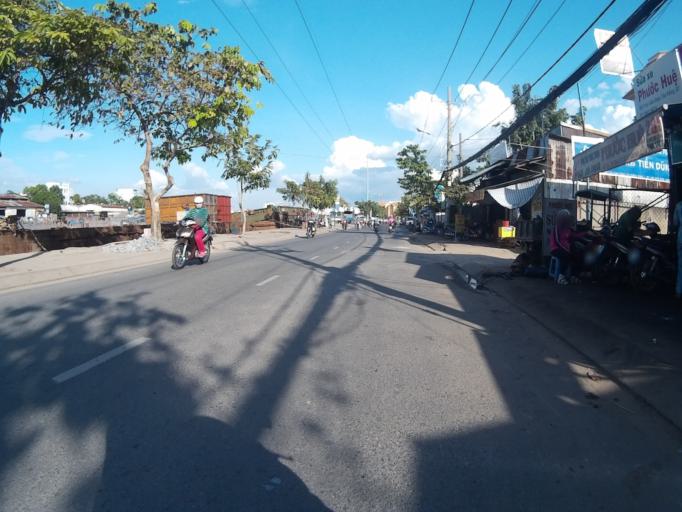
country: VN
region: Ho Chi Minh City
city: Quan Bon
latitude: 10.7518
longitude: 106.7144
